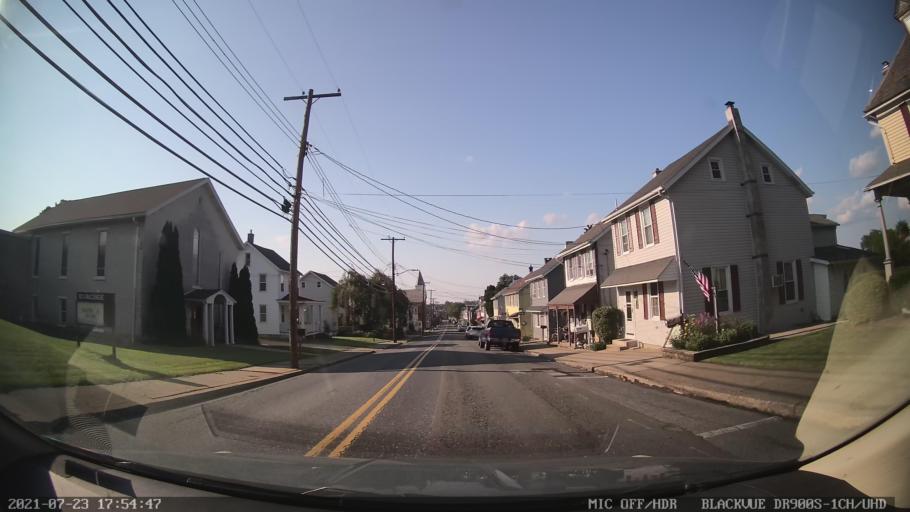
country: US
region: Pennsylvania
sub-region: Lehigh County
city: Macungie
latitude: 40.5117
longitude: -75.5553
